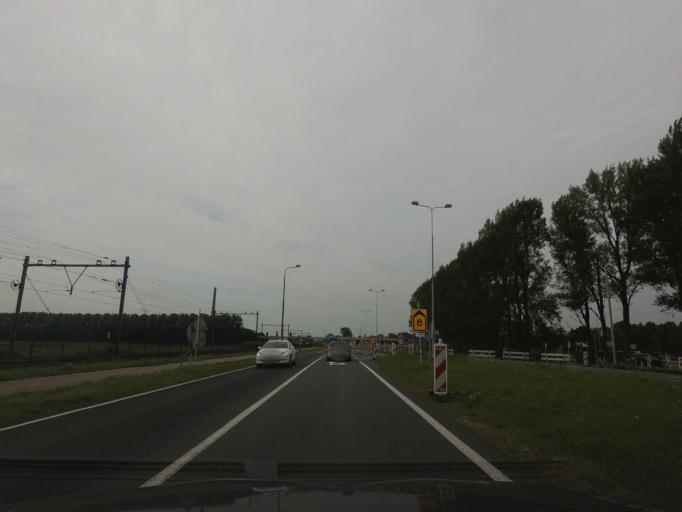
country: NL
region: North Holland
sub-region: Gemeente Zaanstad
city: Zaanstad
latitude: 52.4922
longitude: 4.7803
